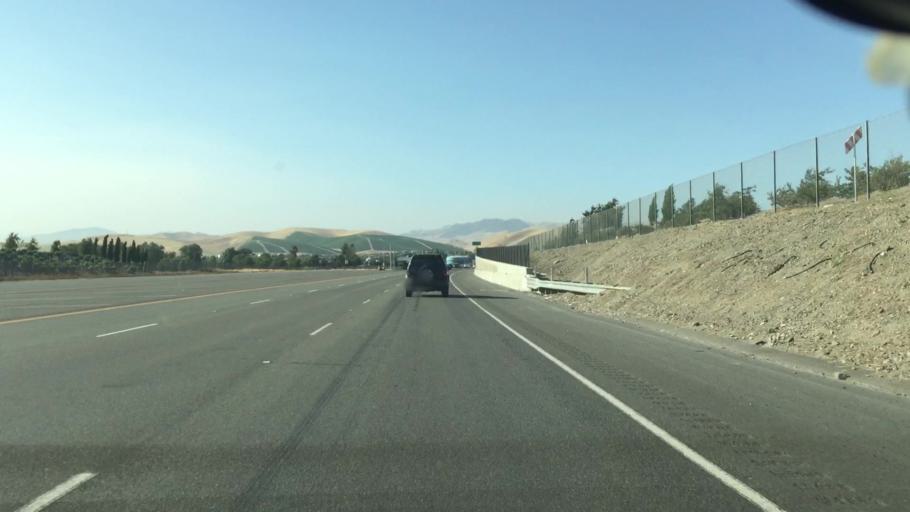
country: US
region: California
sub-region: Alameda County
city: Livermore
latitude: 37.6854
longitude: -121.8055
